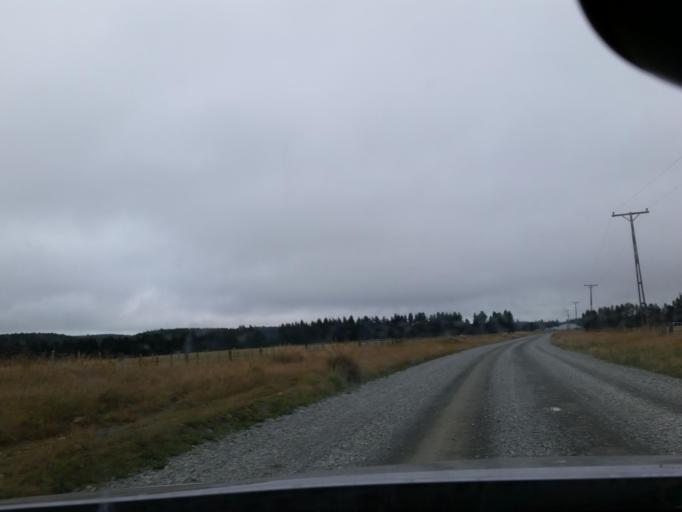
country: NZ
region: Southland
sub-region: Southland District
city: Te Anau
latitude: -45.5461
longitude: 168.1190
